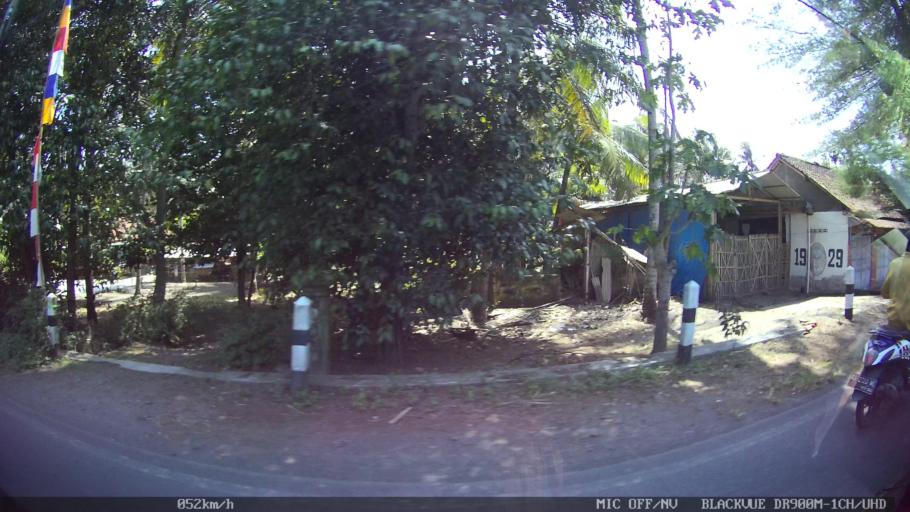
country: ID
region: Daerah Istimewa Yogyakarta
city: Srandakan
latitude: -7.9037
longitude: 110.0752
